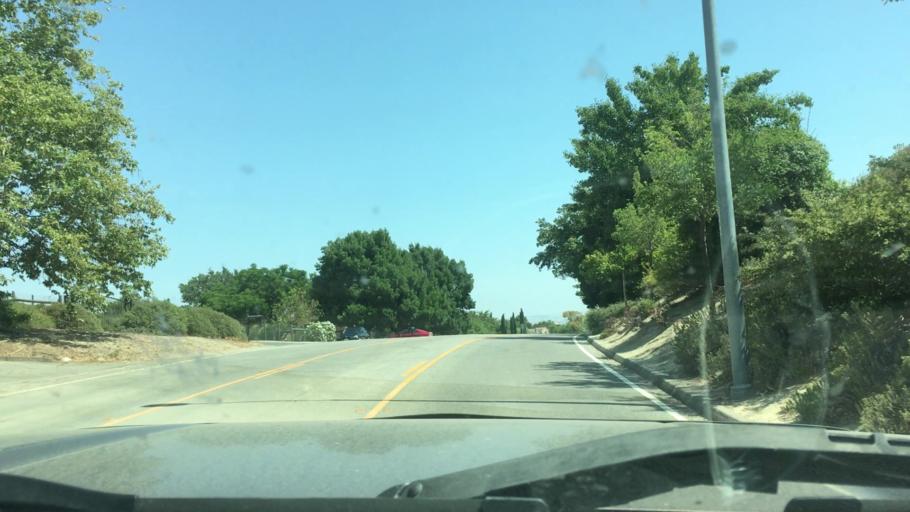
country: US
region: California
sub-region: San Luis Obispo County
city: Paso Robles
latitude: 35.6297
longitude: -120.6610
